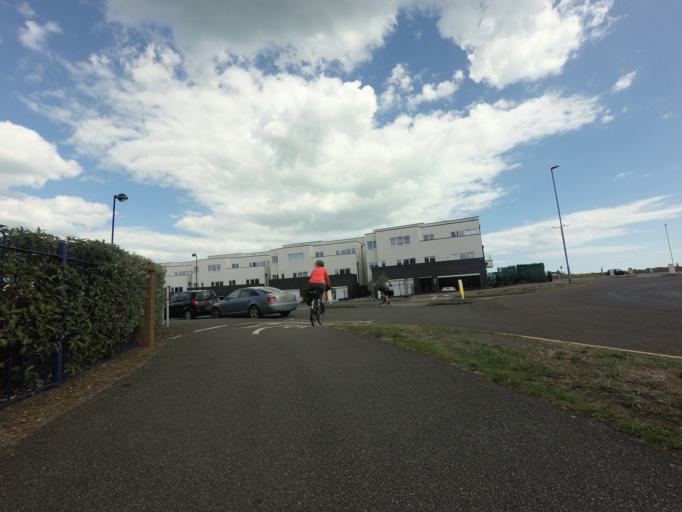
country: GB
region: England
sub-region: East Sussex
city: Pevensey
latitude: 50.7860
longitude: 0.3279
